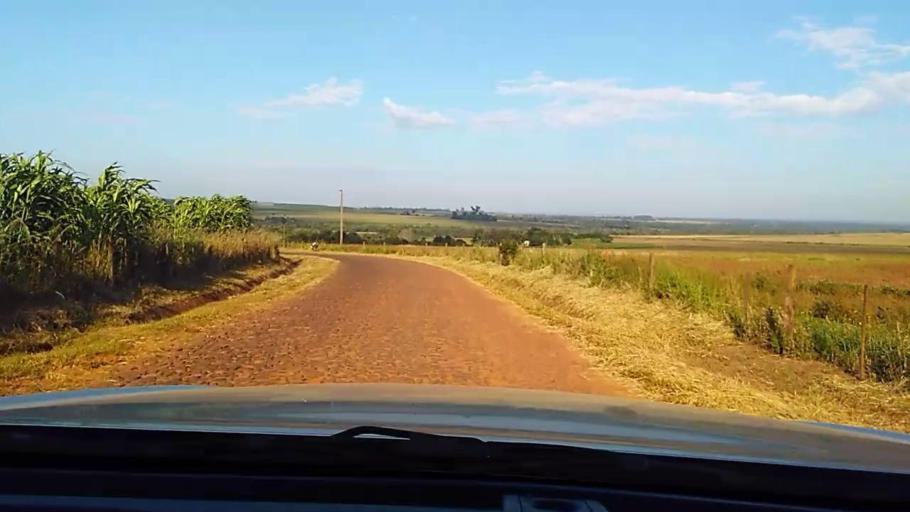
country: PY
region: Alto Parana
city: Doctor Juan Leon Mallorquin
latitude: -25.6962
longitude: -55.3798
